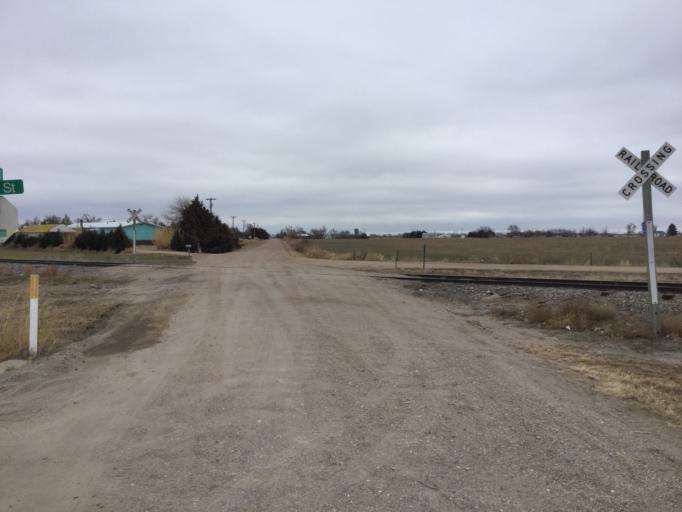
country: US
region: Kansas
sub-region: Pawnee County
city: Larned
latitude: 38.1889
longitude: -99.0837
